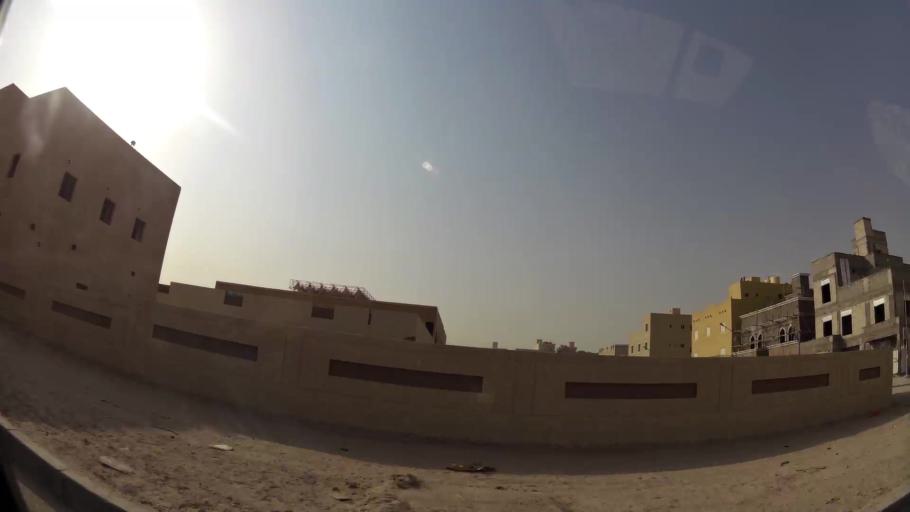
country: KW
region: Al Asimah
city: Ar Rabiyah
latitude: 29.3294
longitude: 47.8046
